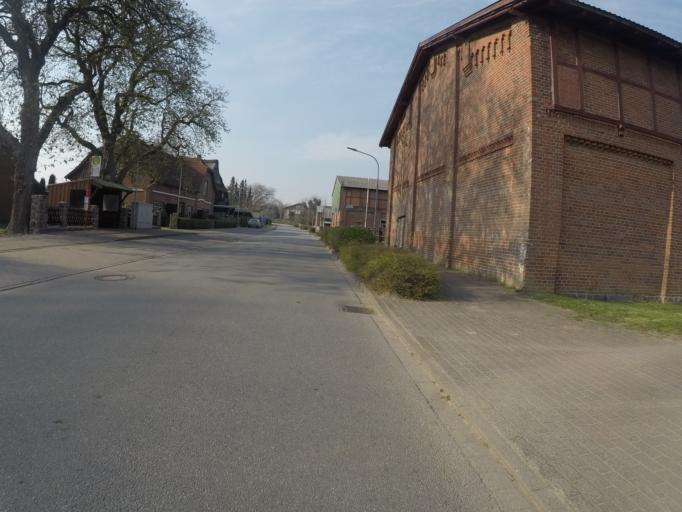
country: DE
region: Schleswig-Holstein
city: Kukels
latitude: 53.8951
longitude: 10.2389
